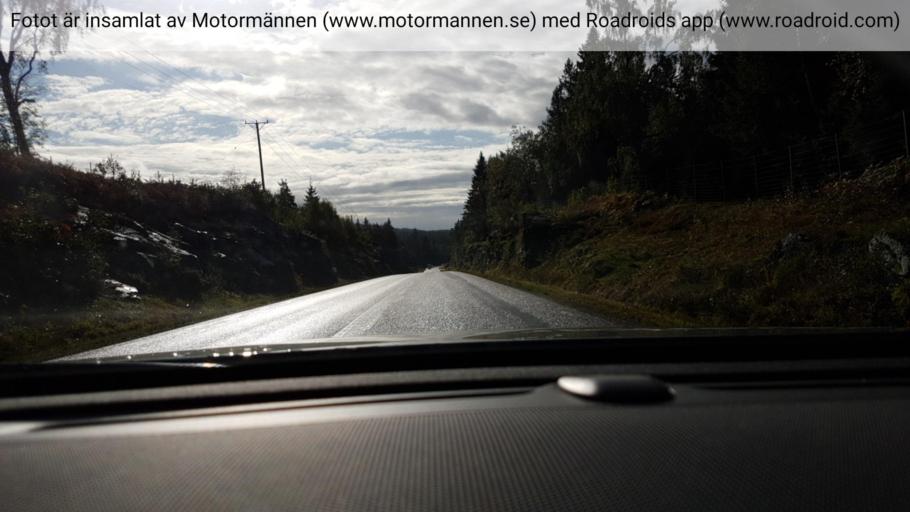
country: SE
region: Vaestra Goetaland
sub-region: Harryda Kommun
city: Hindas
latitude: 57.6511
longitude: 12.3991
